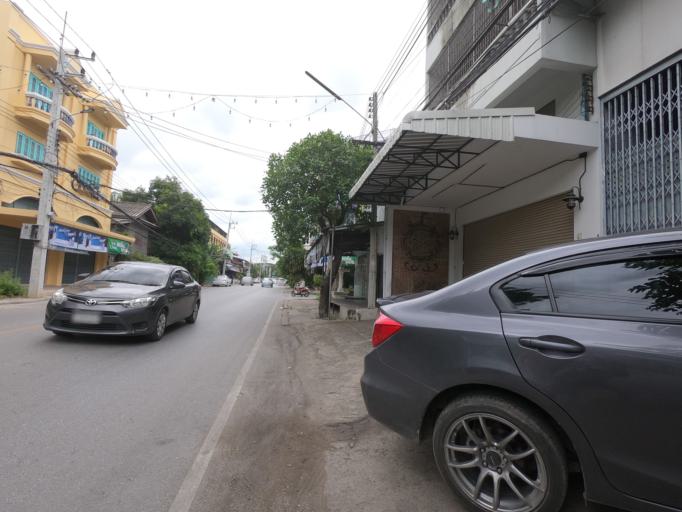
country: TH
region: Nakhon Pathom
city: Nakhon Pathom
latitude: 13.8210
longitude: 100.0503
